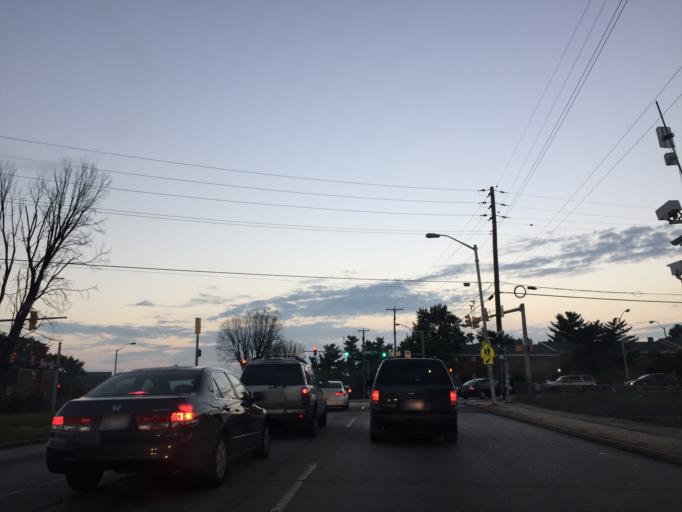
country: US
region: Maryland
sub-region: Baltimore County
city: Rosedale
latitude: 39.3221
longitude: -76.5479
